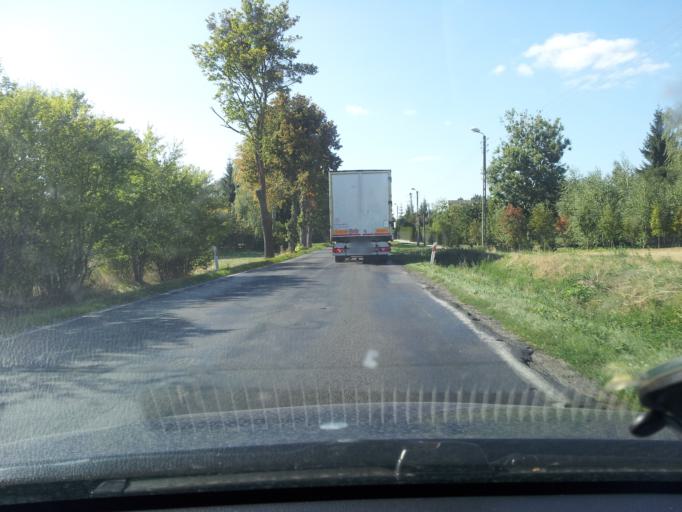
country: PL
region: Kujawsko-Pomorskie
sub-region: Powiat golubsko-dobrzynski
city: Kowalewo Pomorskie
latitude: 53.1515
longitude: 18.9535
